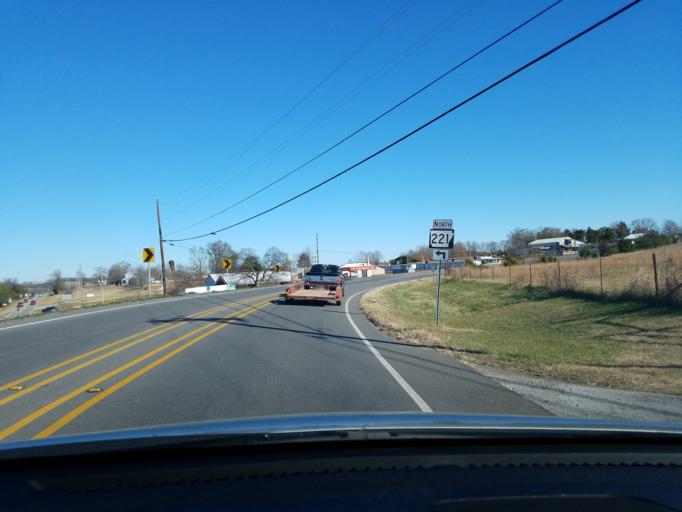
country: US
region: Arkansas
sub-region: Carroll County
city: Berryville
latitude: 36.3914
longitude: -93.5660
